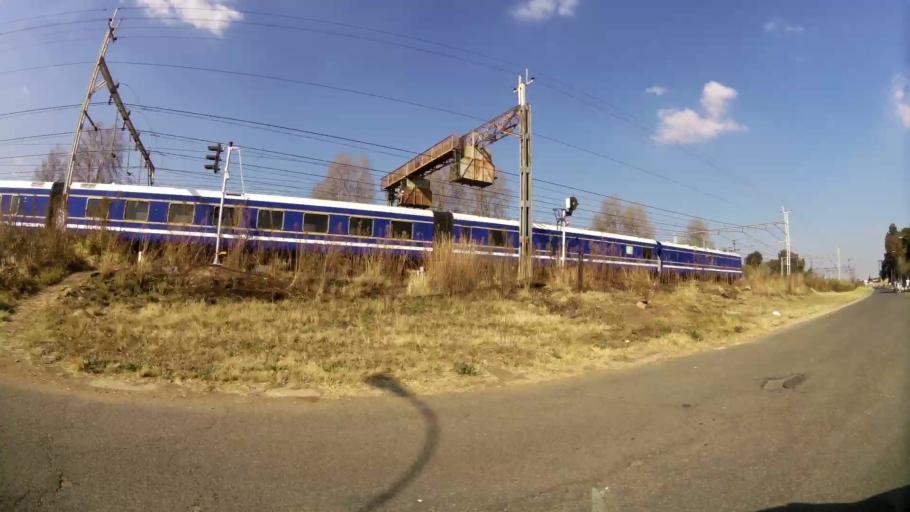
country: ZA
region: Gauteng
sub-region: City of Johannesburg Metropolitan Municipality
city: Modderfontein
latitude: -26.0924
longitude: 28.2207
